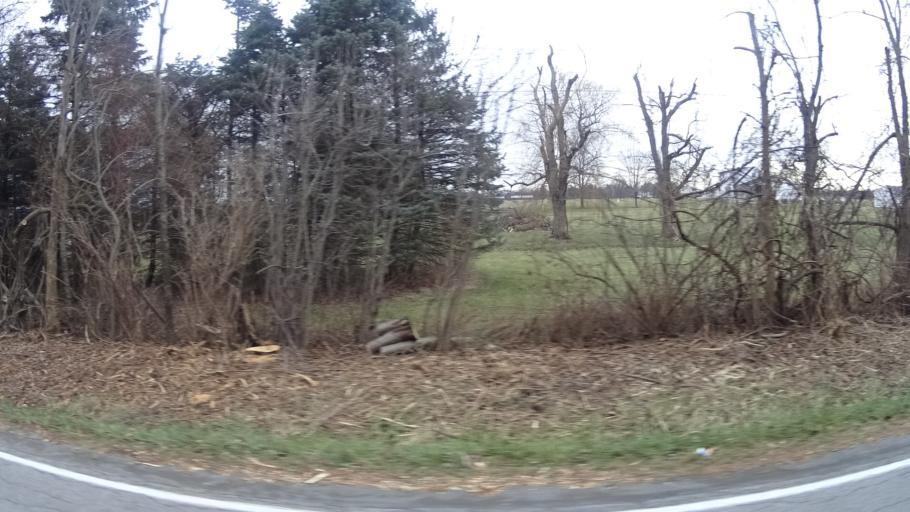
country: US
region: Ohio
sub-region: Lorain County
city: Wellington
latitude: 41.1302
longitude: -82.2693
